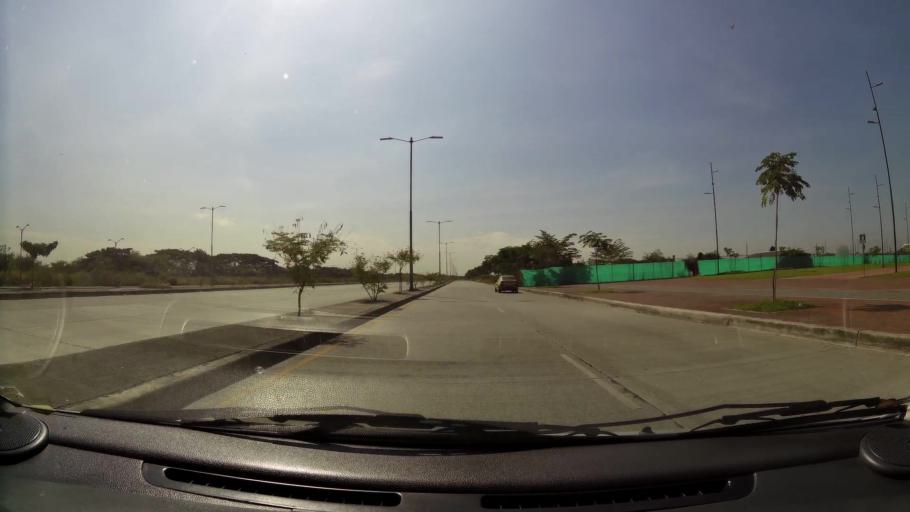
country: EC
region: Guayas
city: Eloy Alfaro
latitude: -2.1009
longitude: -79.9007
